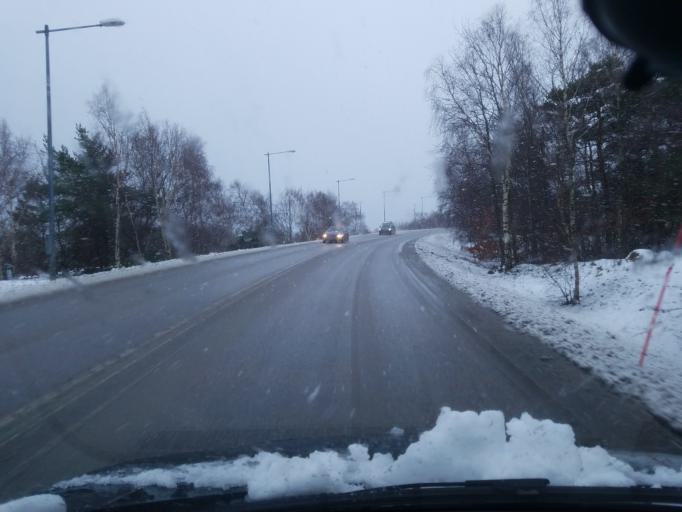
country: SE
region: Vaestra Goetaland
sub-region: Lysekils Kommun
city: Lysekil
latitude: 58.2810
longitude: 11.4654
